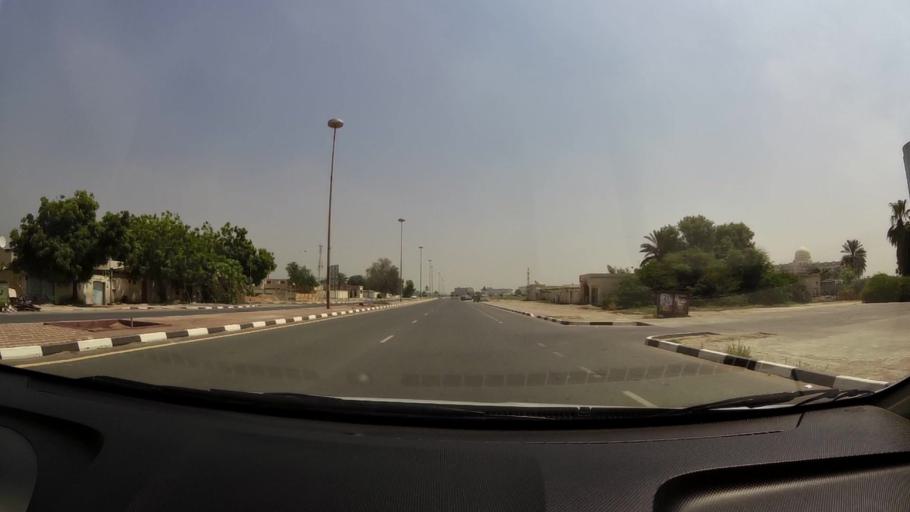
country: AE
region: Umm al Qaywayn
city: Umm al Qaywayn
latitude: 25.5712
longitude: 55.5607
